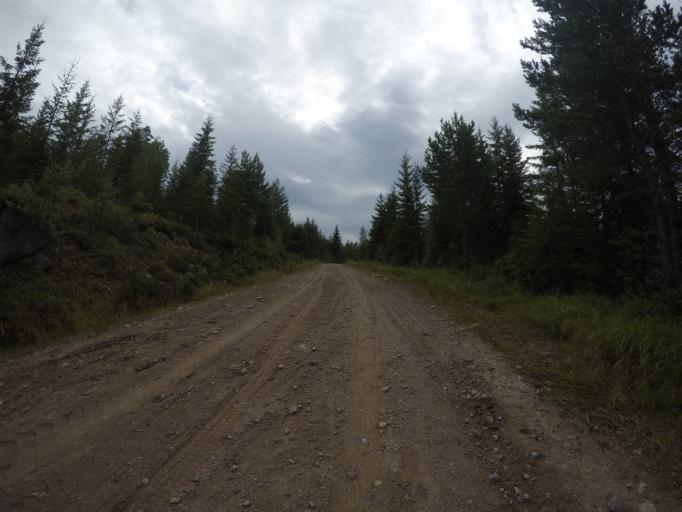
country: SE
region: OErebro
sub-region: Hallefors Kommun
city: Haellefors
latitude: 60.0164
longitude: 14.4710
